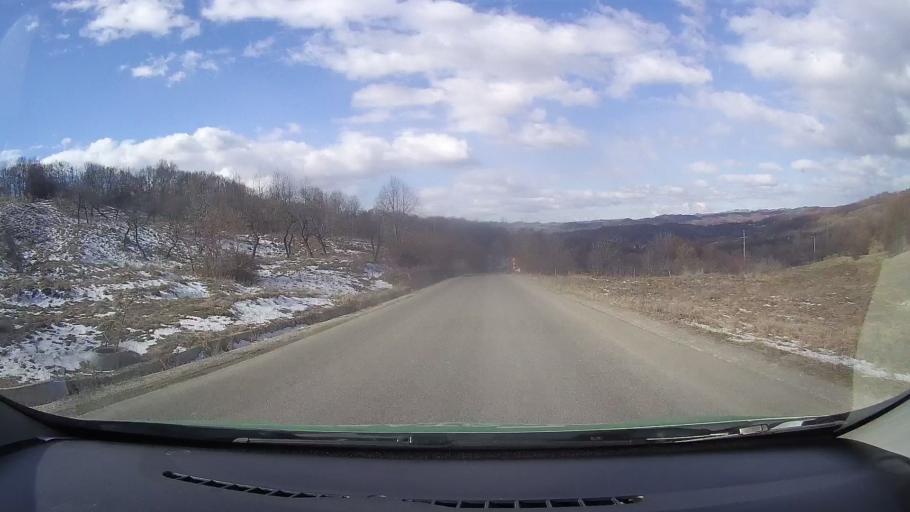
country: RO
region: Dambovita
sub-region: Oras Pucioasa
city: Glodeni
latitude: 45.0909
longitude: 25.4710
